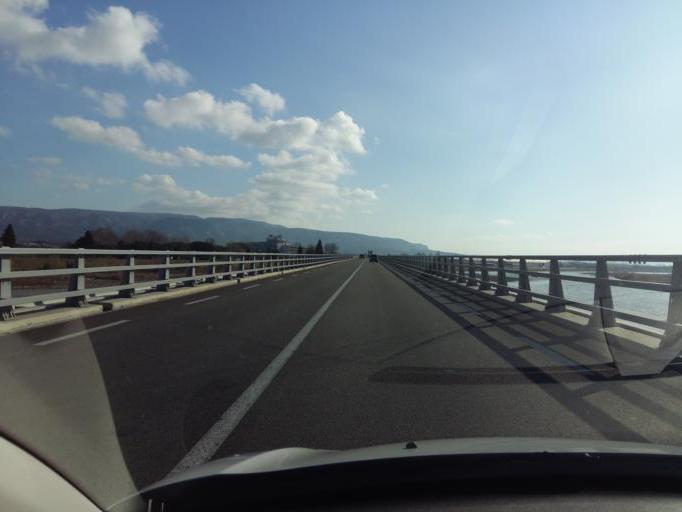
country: FR
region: Provence-Alpes-Cote d'Azur
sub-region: Departement du Vaucluse
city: Cavaillon
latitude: 43.8205
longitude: 5.0335
